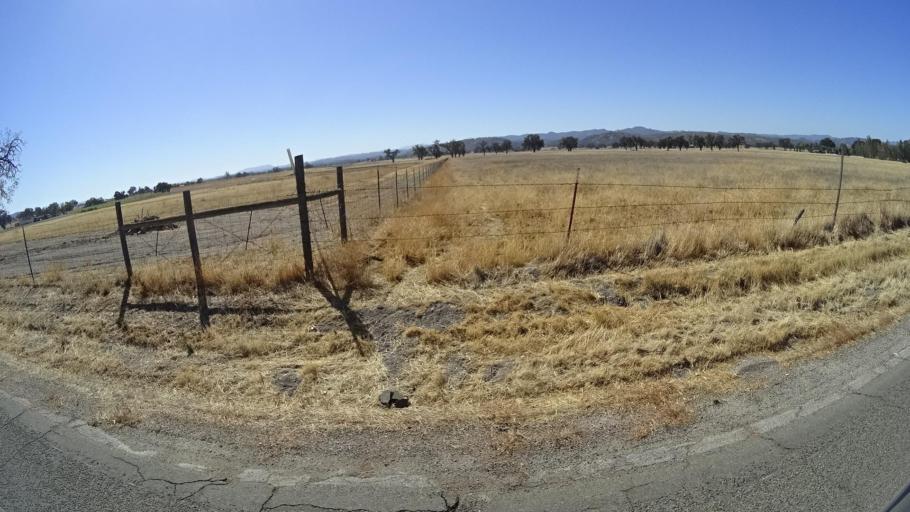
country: US
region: California
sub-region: Monterey County
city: King City
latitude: 35.9443
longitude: -121.0779
